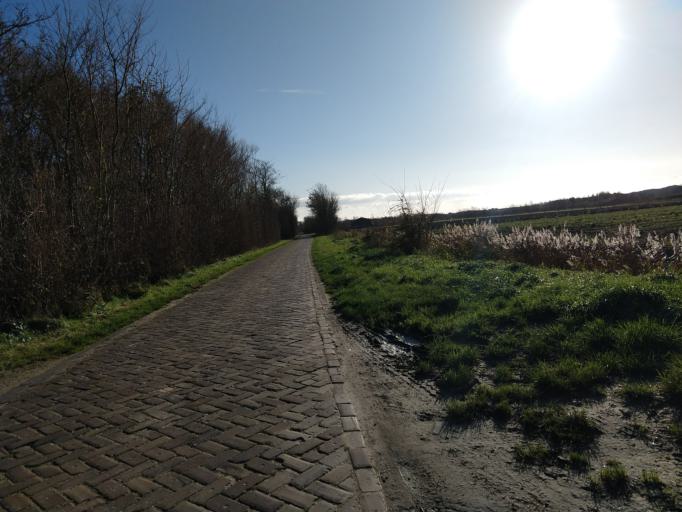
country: NL
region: Zeeland
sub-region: Gemeente Vlissingen
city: Vlissingen
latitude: 51.5109
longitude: 3.4850
